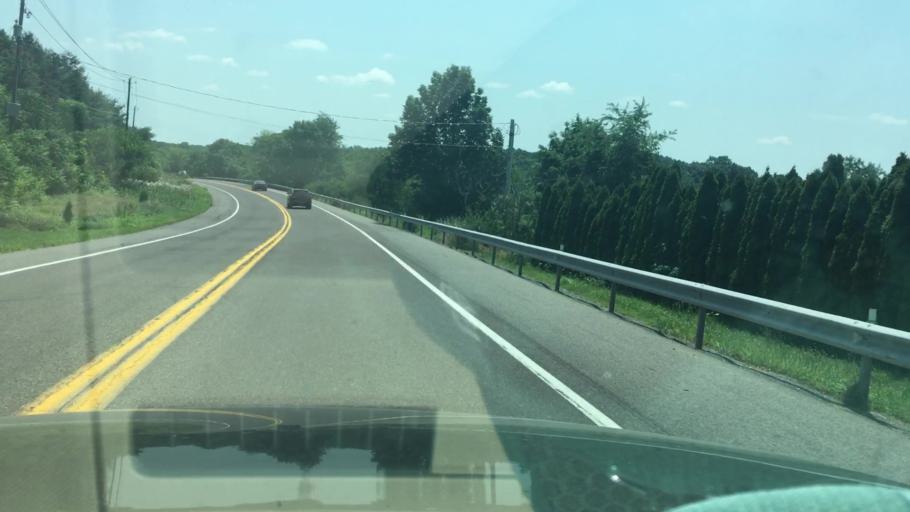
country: US
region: Pennsylvania
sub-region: Lehigh County
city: Trexlertown
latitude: 40.6043
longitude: -75.6404
